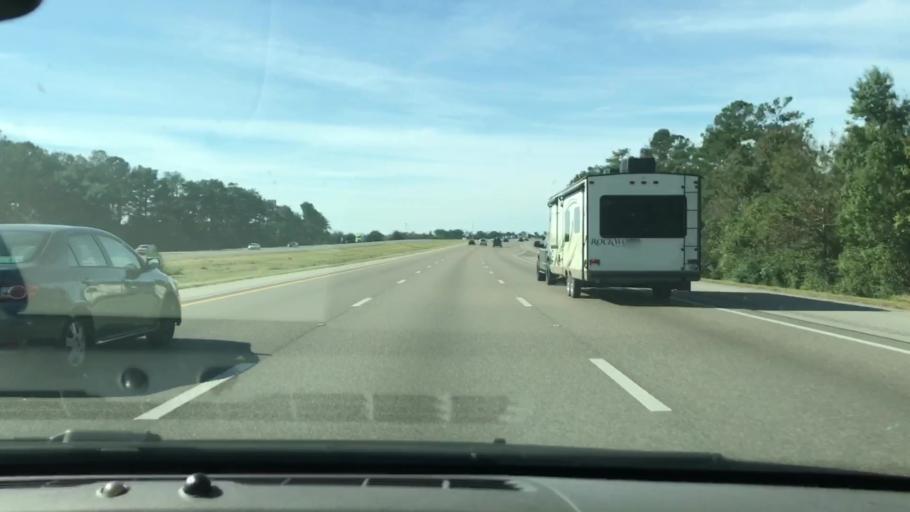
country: US
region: Mississippi
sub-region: Harrison County
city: D'Iberville
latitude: 30.4480
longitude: -88.9277
